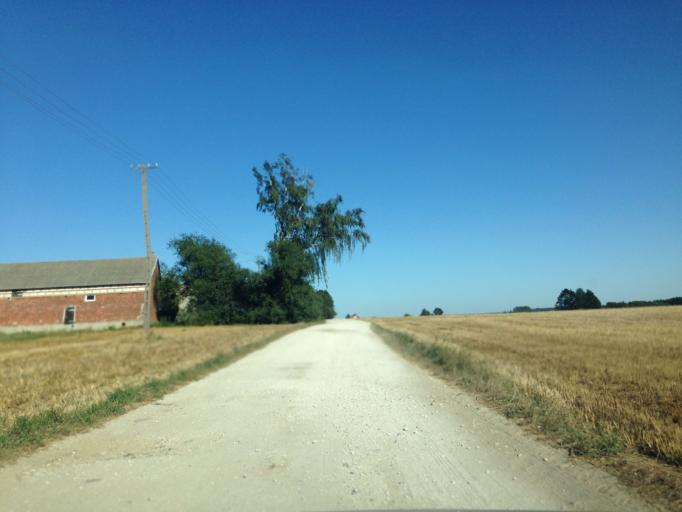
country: PL
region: Kujawsko-Pomorskie
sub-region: Powiat brodnicki
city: Swiedziebnia
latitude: 53.1900
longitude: 19.5692
